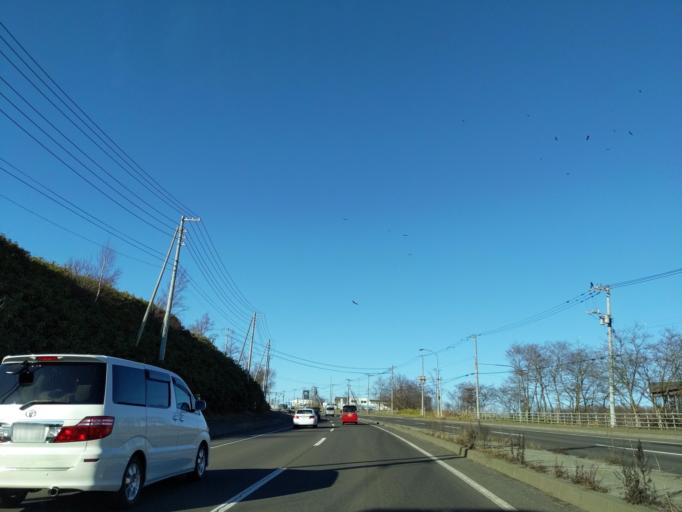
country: JP
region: Hokkaido
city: Kitahiroshima
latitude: 42.9583
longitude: 141.4950
